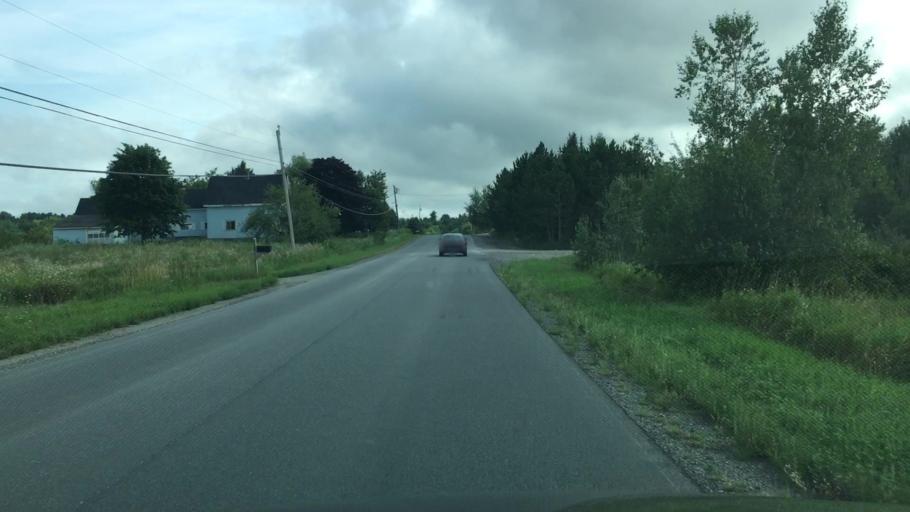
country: US
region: Maine
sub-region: Waldo County
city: Winterport
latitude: 44.6719
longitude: -68.8684
